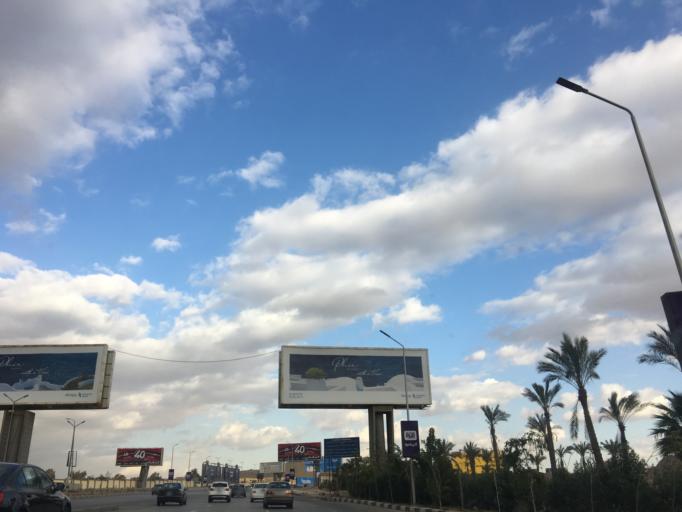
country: EG
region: Muhafazat al Qahirah
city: Cairo
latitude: 30.0240
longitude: 31.3578
